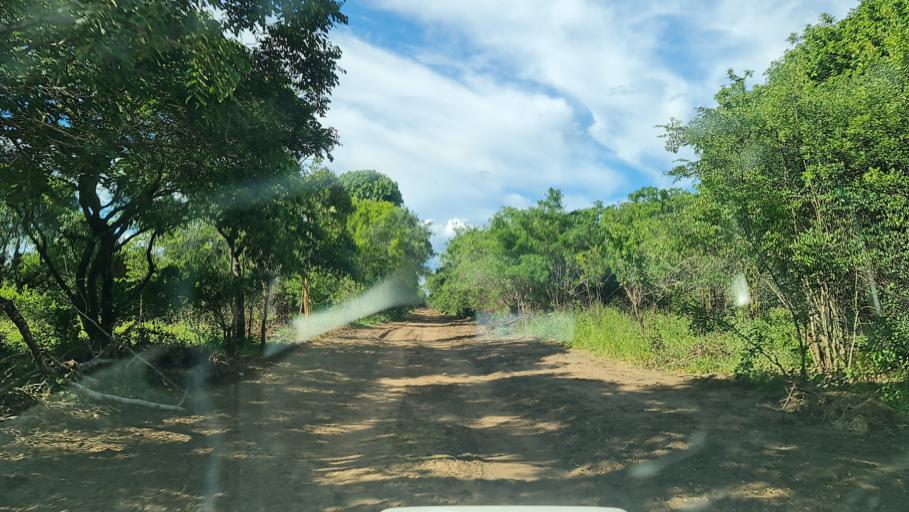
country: MZ
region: Nampula
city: Antonio Enes
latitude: -15.5208
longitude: 40.1285
